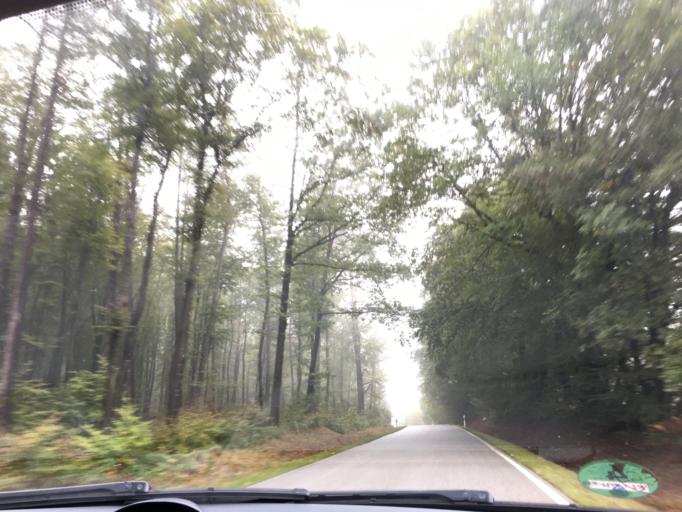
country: DE
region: Rheinland-Pfalz
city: Schmalenberg
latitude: 49.3206
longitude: 7.7586
